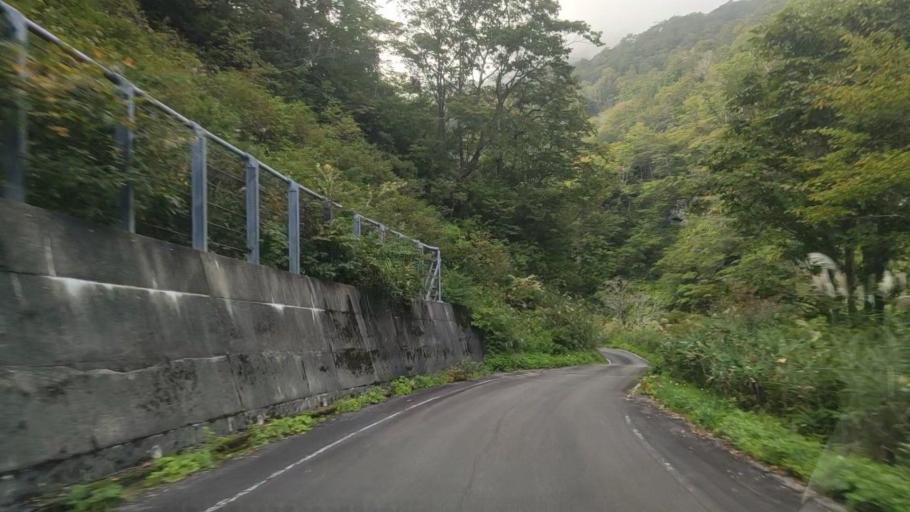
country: JP
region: Toyama
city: Yatsuomachi-higashikumisaka
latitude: 36.3855
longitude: 137.0845
